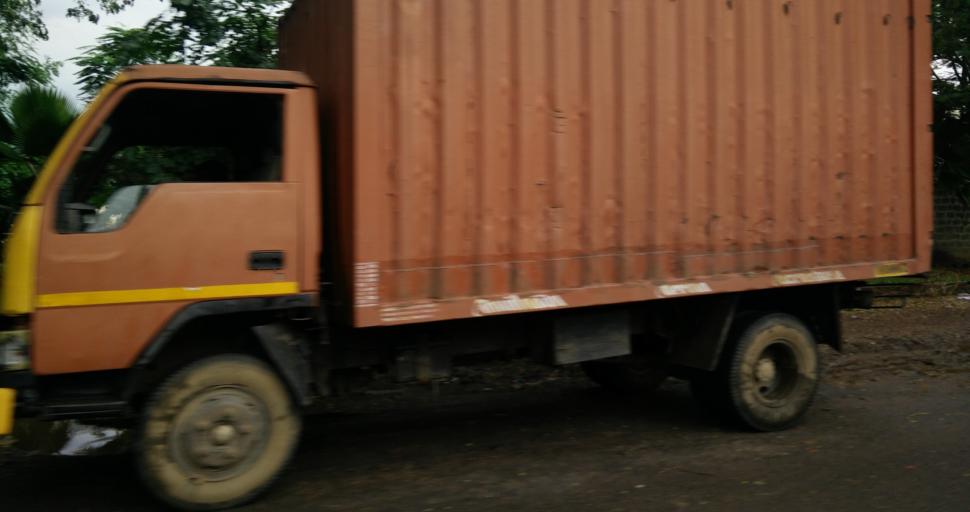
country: IN
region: Tamil Nadu
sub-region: Kancheepuram
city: Nandambakkam
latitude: 12.9995
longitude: 80.0222
